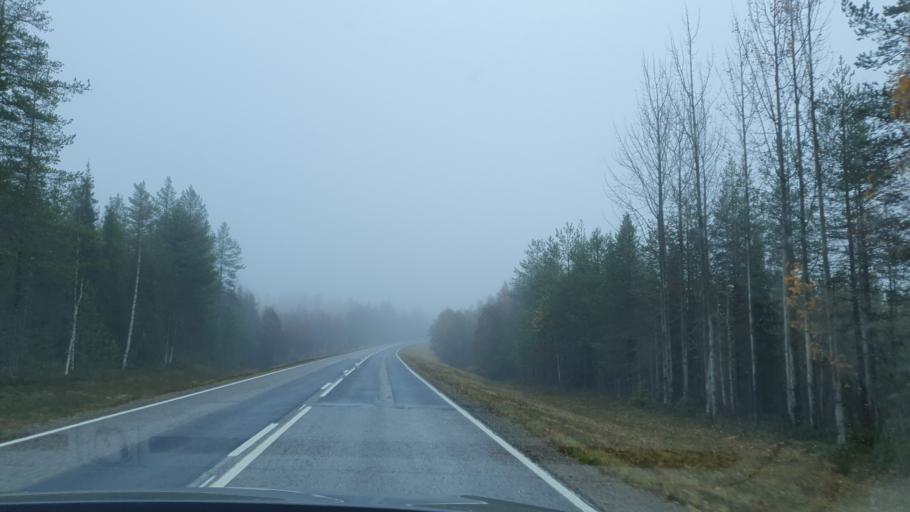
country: FI
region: Lapland
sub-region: Tunturi-Lappi
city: Kittilae
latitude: 67.3127
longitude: 24.9107
